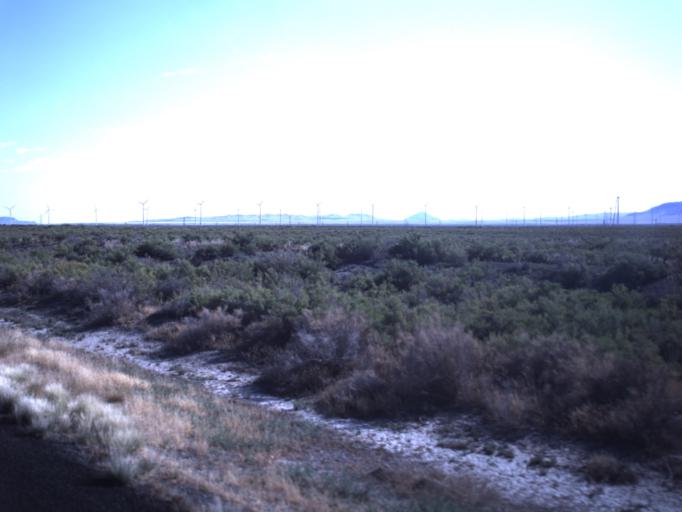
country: US
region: Utah
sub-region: Beaver County
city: Milford
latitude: 38.5527
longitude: -112.9912
